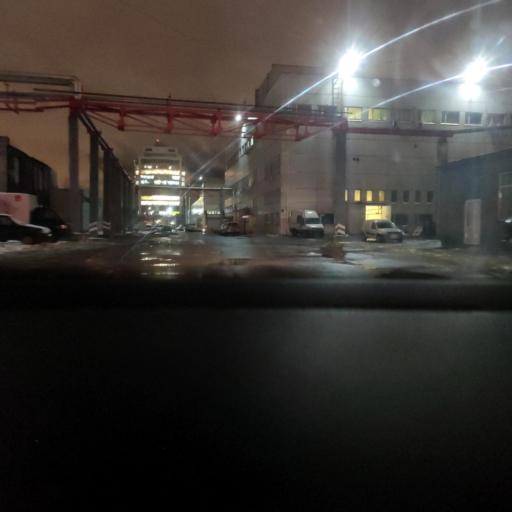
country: RU
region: Moskovskaya
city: Presnenskiy
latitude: 55.7344
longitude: 37.5505
